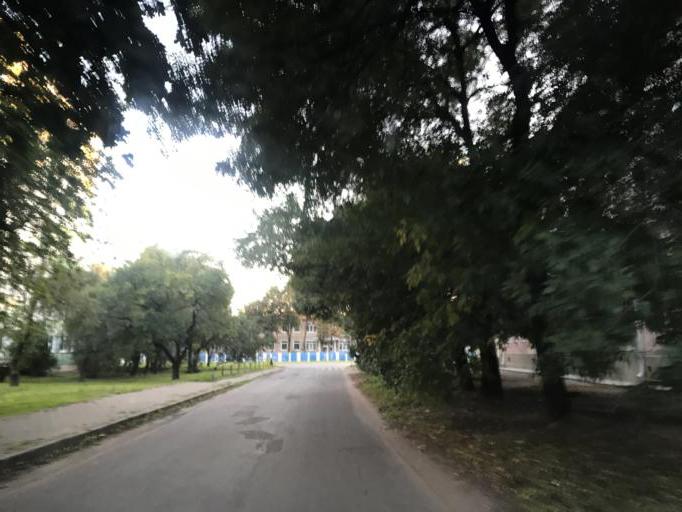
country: BY
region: Mogilev
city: Mahilyow
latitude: 53.9079
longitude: 30.3205
